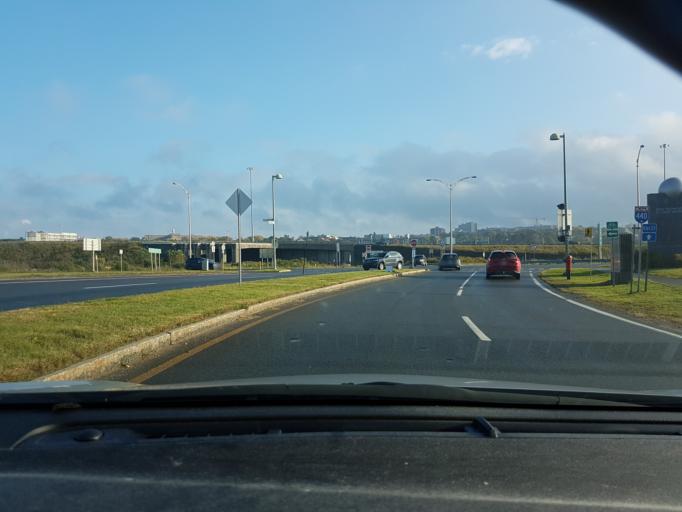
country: CA
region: Quebec
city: L'Ancienne-Lorette
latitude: 46.7955
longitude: -71.2929
